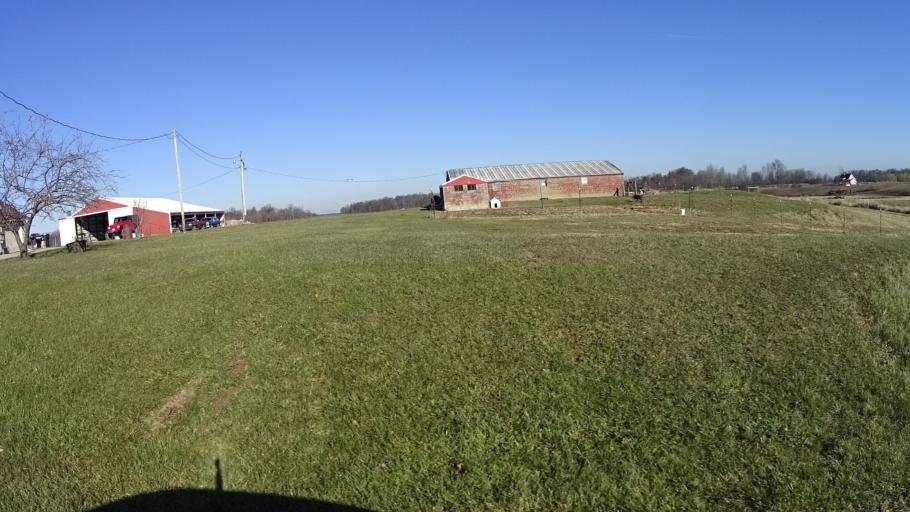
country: US
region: Ohio
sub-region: Lorain County
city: Wellington
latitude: 41.0708
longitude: -82.2454
